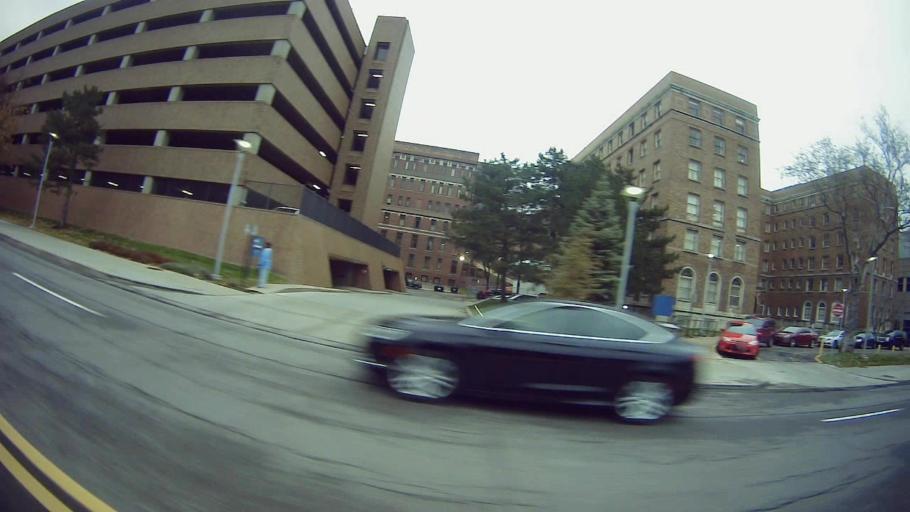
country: US
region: Michigan
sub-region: Wayne County
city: Detroit
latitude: 42.3500
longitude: -83.0571
